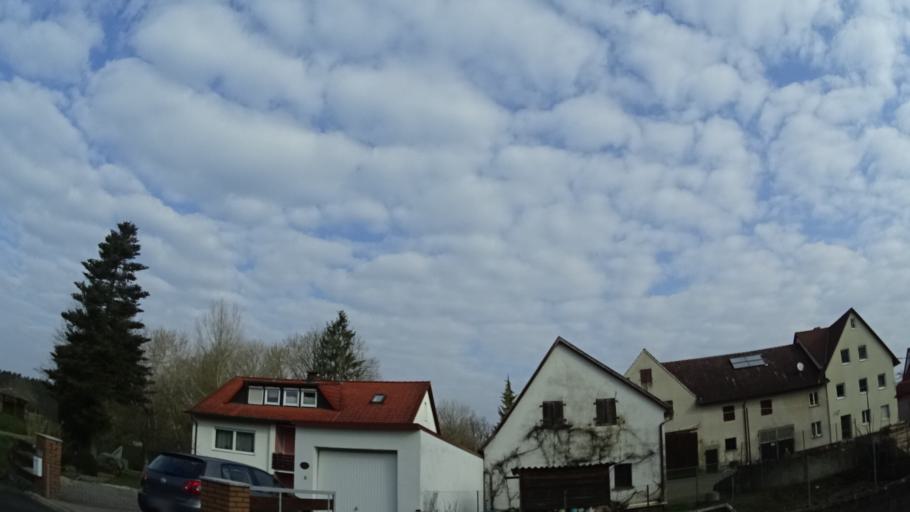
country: DE
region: Bavaria
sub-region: Regierungsbezirk Mittelfranken
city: Altdorf
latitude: 49.3998
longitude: 11.3358
